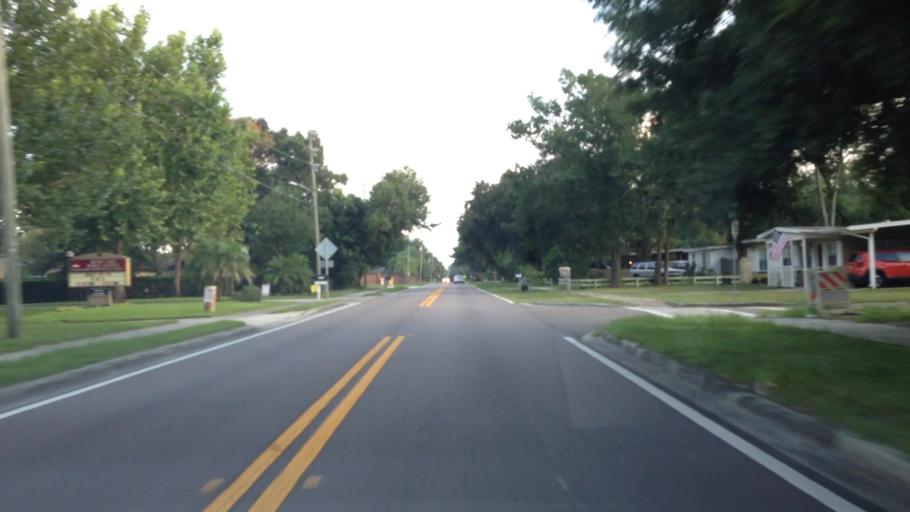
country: US
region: Florida
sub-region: Seminole County
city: Forest City
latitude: 28.6612
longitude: -81.4439
